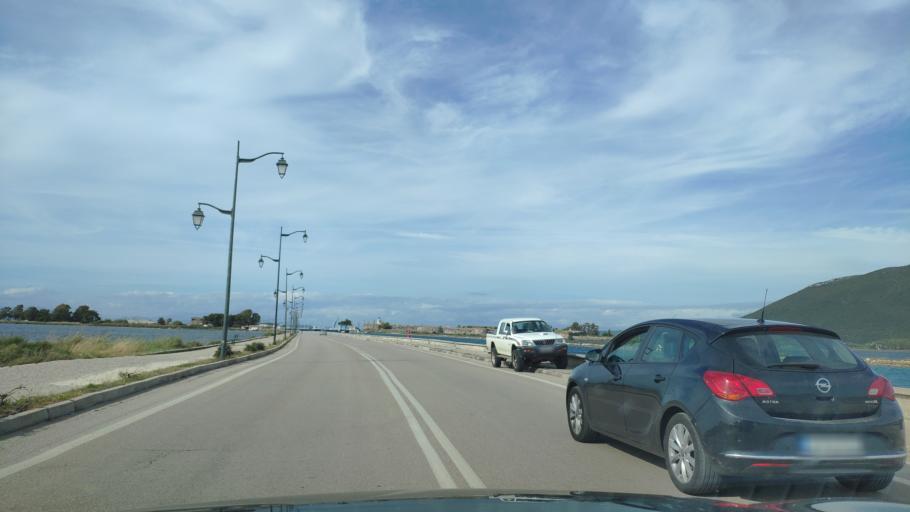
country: GR
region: Ionian Islands
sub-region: Lefkada
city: Lefkada
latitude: 38.8390
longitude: 20.7143
